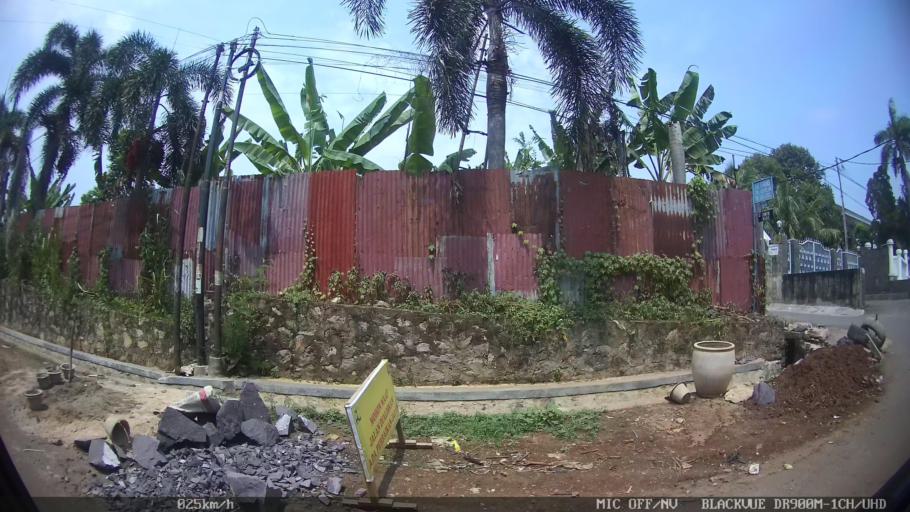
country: ID
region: Lampung
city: Bandarlampung
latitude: -5.4369
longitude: 105.2721
